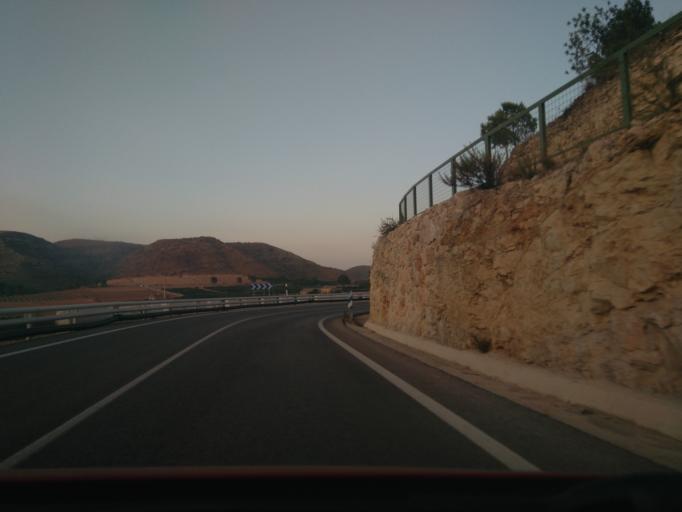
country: ES
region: Valencia
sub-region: Provincia de Valencia
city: Sumacarcer
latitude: 39.0907
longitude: -0.6282
